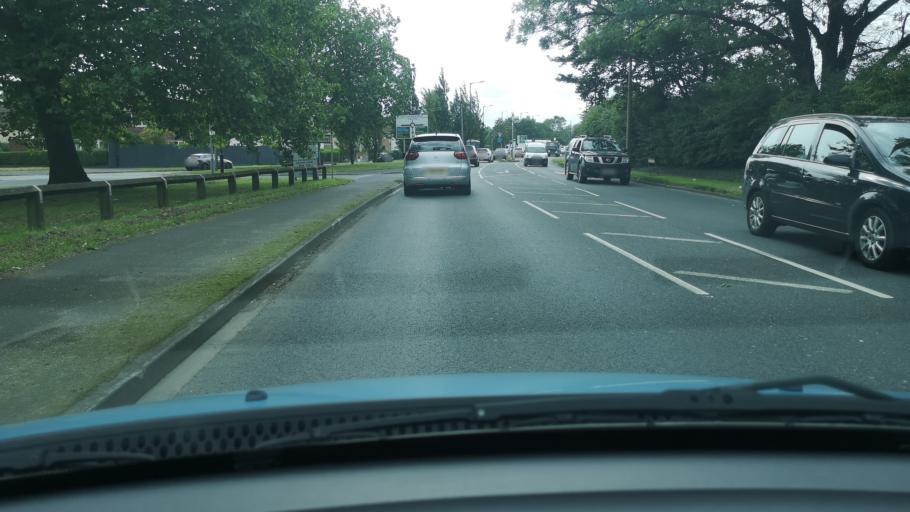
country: GB
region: England
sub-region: Doncaster
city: Kirk Sandall
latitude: 53.5500
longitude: -1.0863
